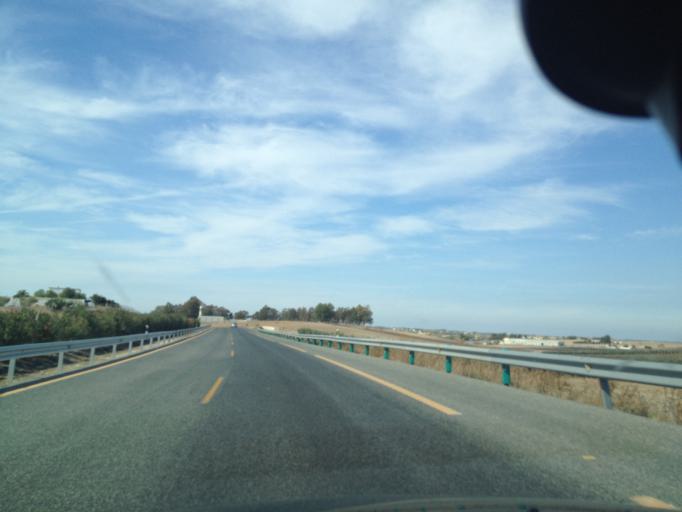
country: ES
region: Andalusia
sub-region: Provincia de Sevilla
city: La Puebla de Cazalla
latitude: 37.2264
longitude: -5.2839
